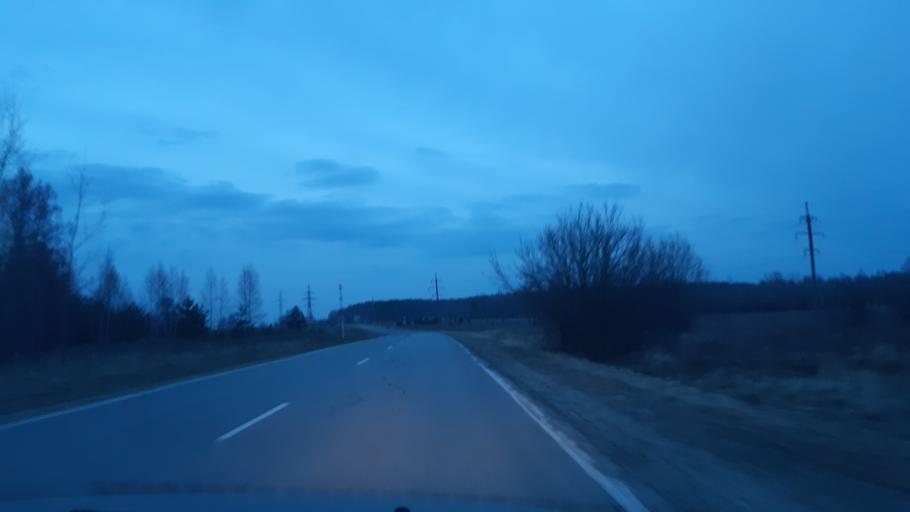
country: RU
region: Vladimir
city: Luknovo
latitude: 56.1938
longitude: 42.0300
